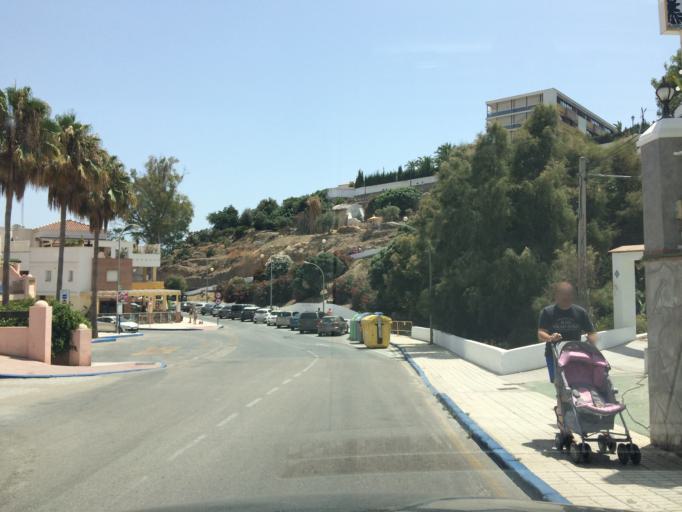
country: ES
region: Andalusia
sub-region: Provincia de Malaga
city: Nerja
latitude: 36.7515
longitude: -3.8697
